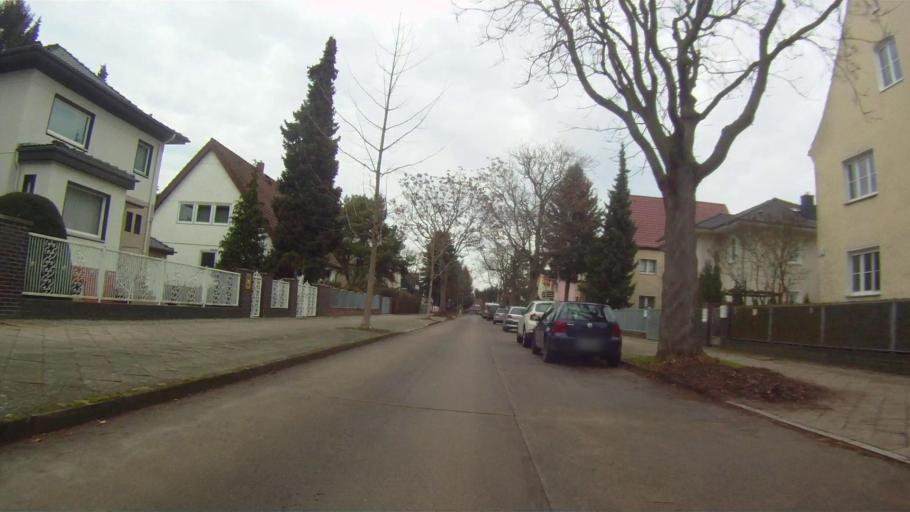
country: DE
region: Berlin
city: Lichtenrade
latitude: 52.3873
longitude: 13.3904
